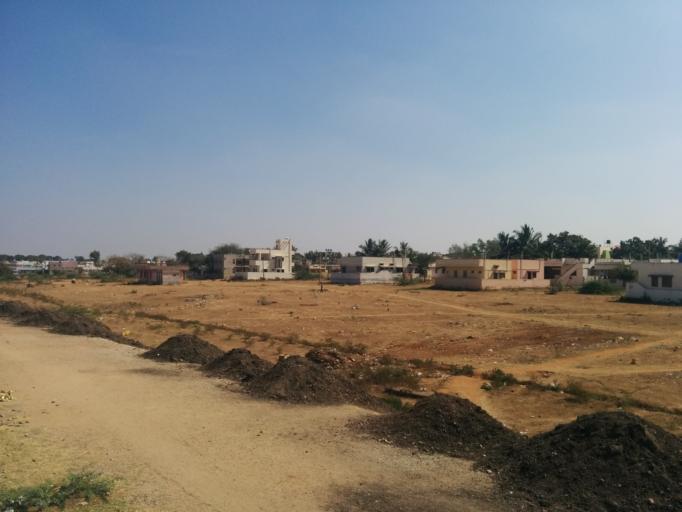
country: IN
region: Karnataka
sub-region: Gadag
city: Gadag
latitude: 15.4375
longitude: 75.6527
